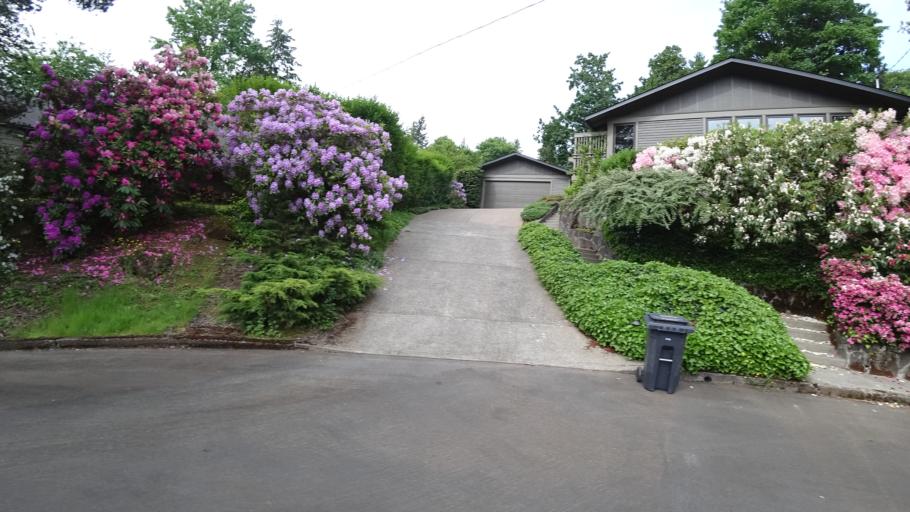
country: US
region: Oregon
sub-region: Clackamas County
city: Lake Oswego
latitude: 45.4264
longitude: -122.6814
